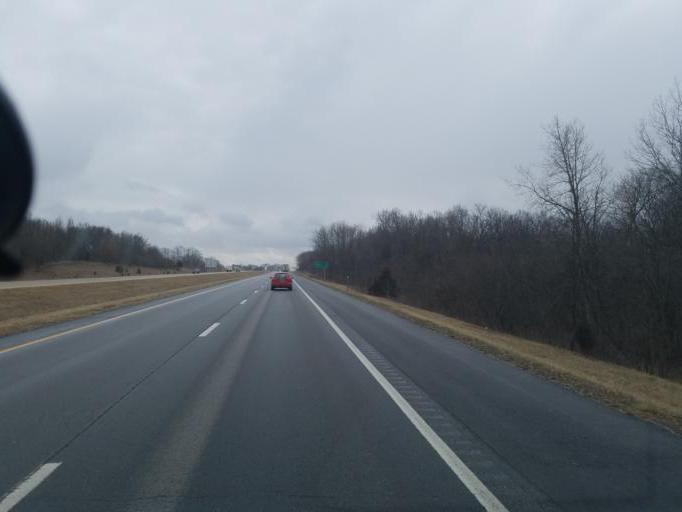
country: US
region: Missouri
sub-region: Randolph County
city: Moberly
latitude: 39.3868
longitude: -92.4135
